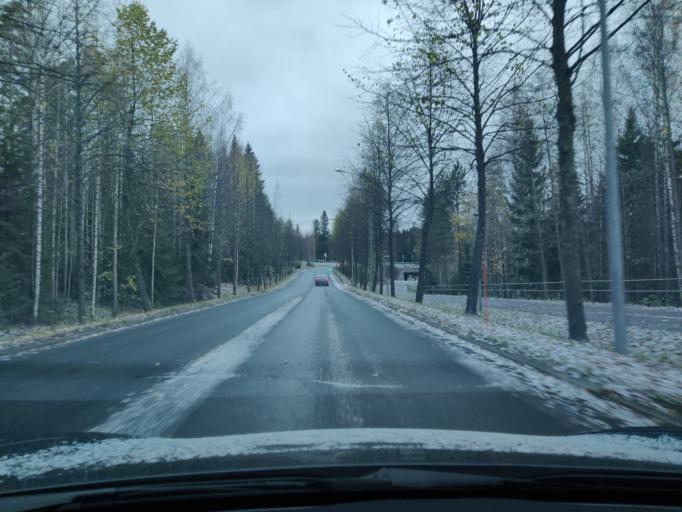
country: FI
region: Northern Savo
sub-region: Kuopio
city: Kuopio
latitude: 62.8403
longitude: 27.6349
